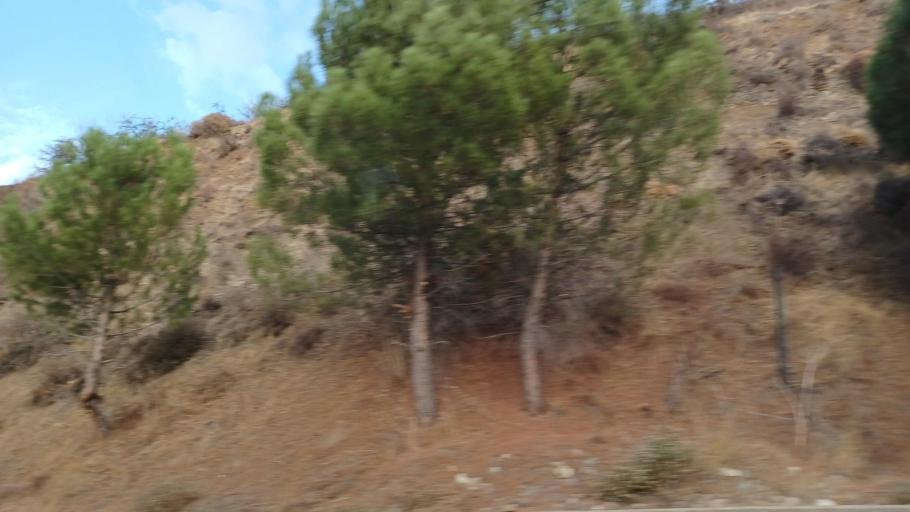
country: CY
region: Lefkosia
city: Kakopetria
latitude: 34.9995
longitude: 32.8998
